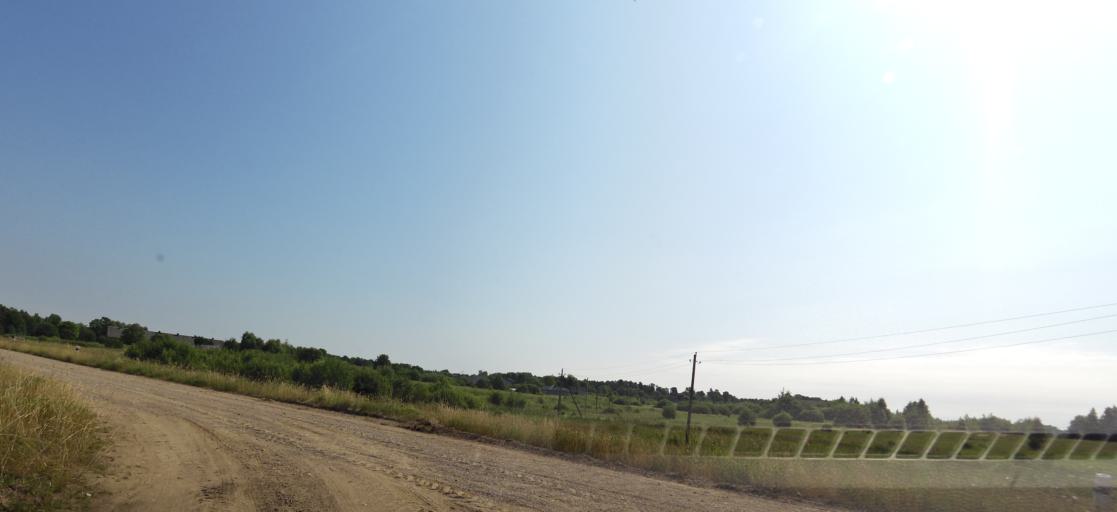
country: LT
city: Grigiskes
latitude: 54.8636
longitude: 25.0629
